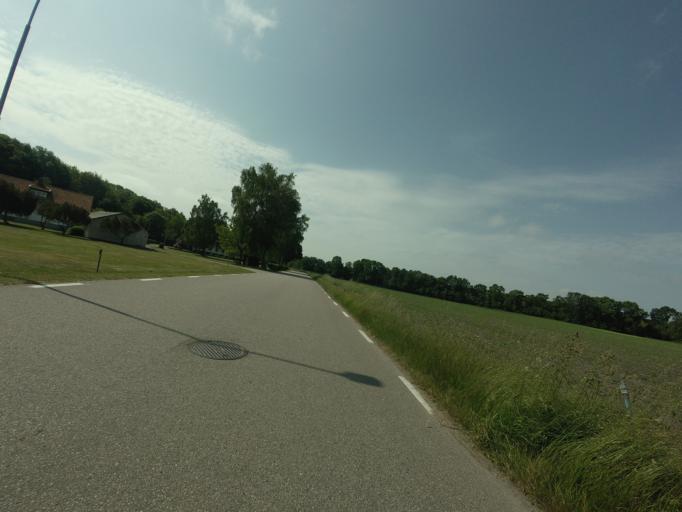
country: SE
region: Skane
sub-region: Helsingborg
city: Odakra
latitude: 56.2146
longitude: 12.7107
